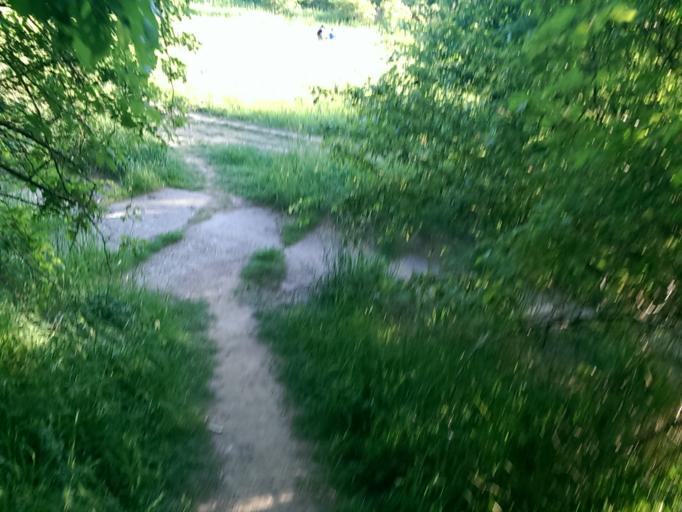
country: CZ
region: Central Bohemia
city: Vestec
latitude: 50.0449
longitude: 14.5023
